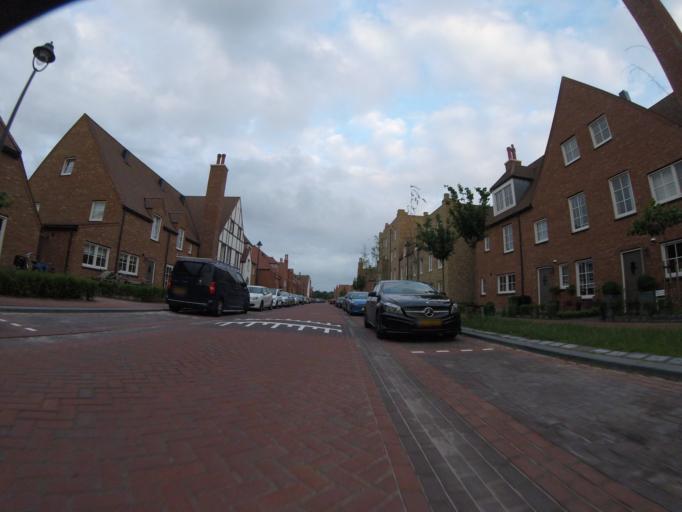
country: NL
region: North Holland
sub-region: Gemeente Haarlemmermeer
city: Hoofddorp
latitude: 52.2942
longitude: 4.6592
